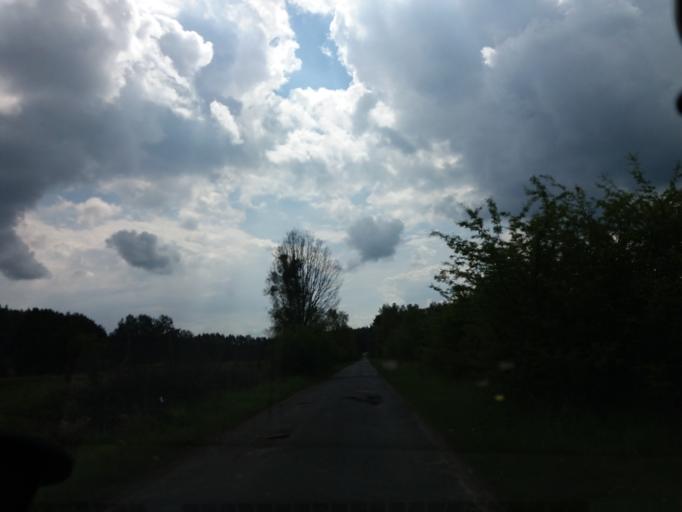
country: PL
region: West Pomeranian Voivodeship
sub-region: Powiat choszczenski
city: Drawno
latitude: 53.1302
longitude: 15.8470
